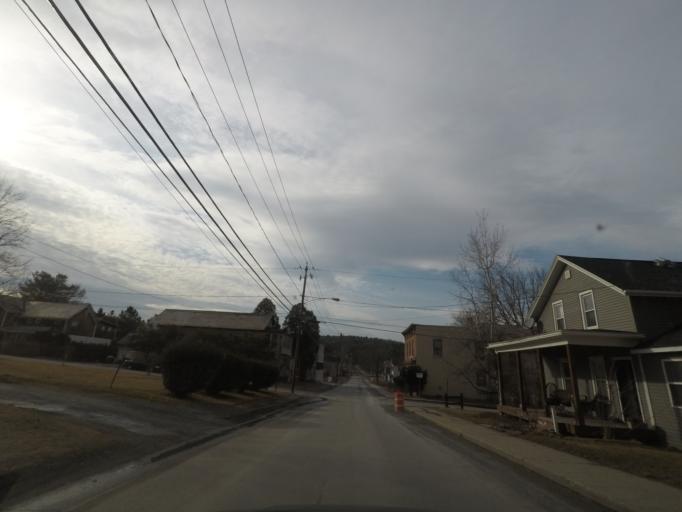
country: US
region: New York
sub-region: Rensselaer County
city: Hoosick Falls
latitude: 42.9072
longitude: -73.3574
